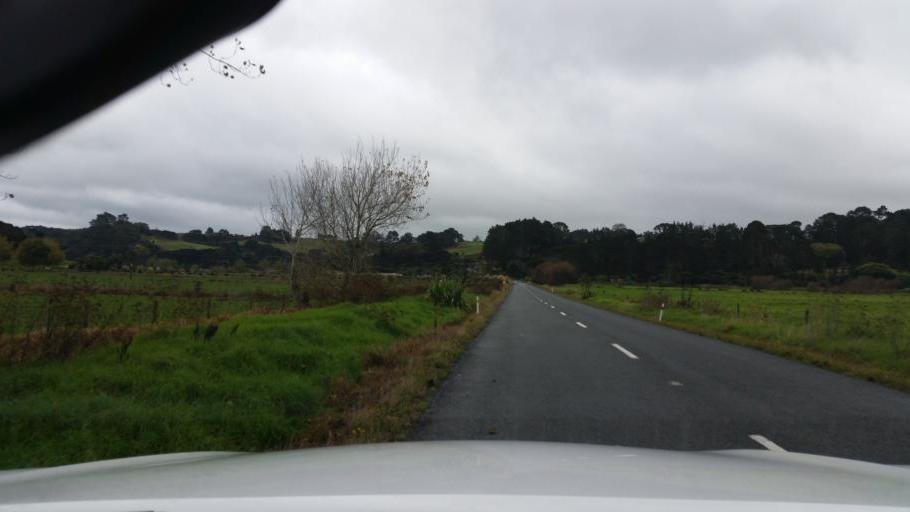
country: NZ
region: Northland
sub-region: Kaipara District
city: Dargaville
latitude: -36.1440
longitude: 173.9836
